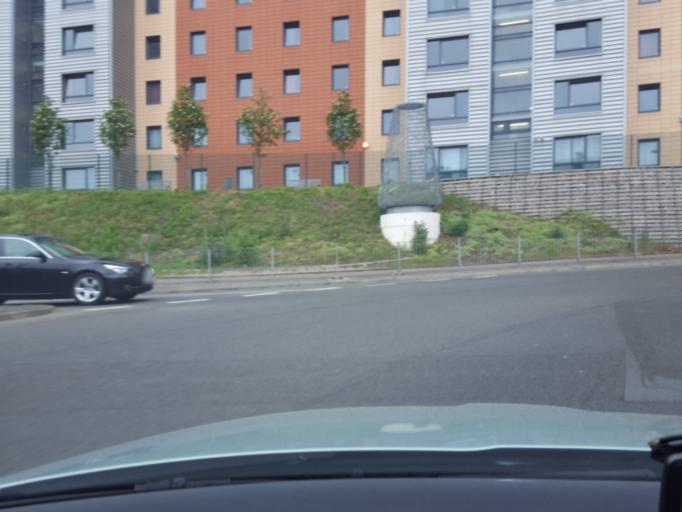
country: GB
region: Scotland
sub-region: Dundee City
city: Dundee
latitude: 56.4636
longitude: -2.9800
